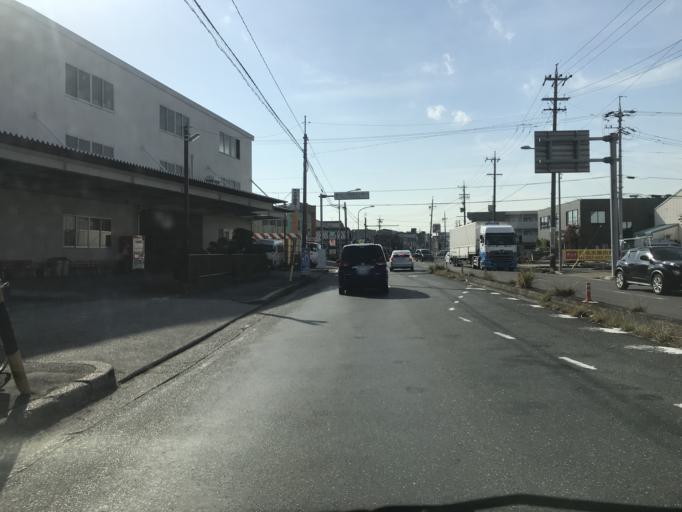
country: JP
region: Aichi
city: Nagoya-shi
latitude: 35.2053
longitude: 136.8687
